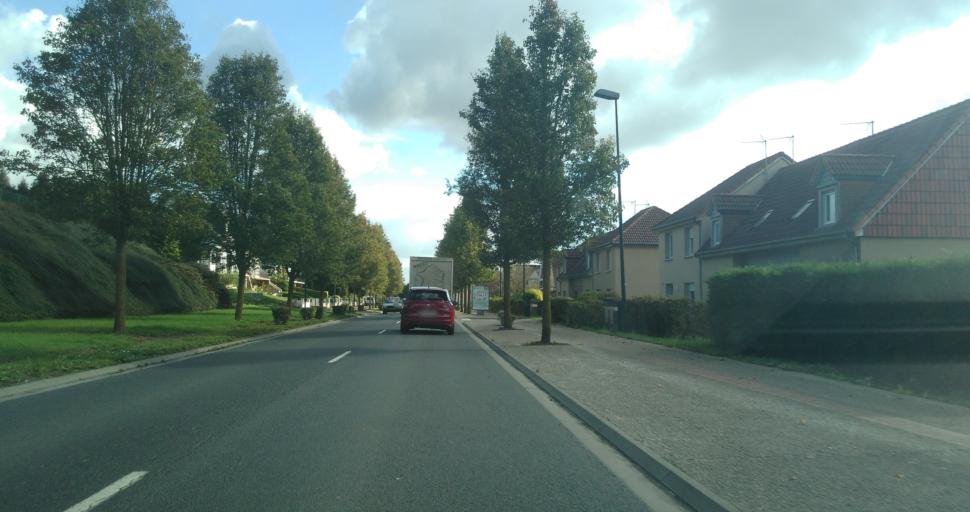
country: FR
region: Picardie
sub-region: Departement de la Somme
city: Doullens
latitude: 50.1624
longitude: 2.3287
